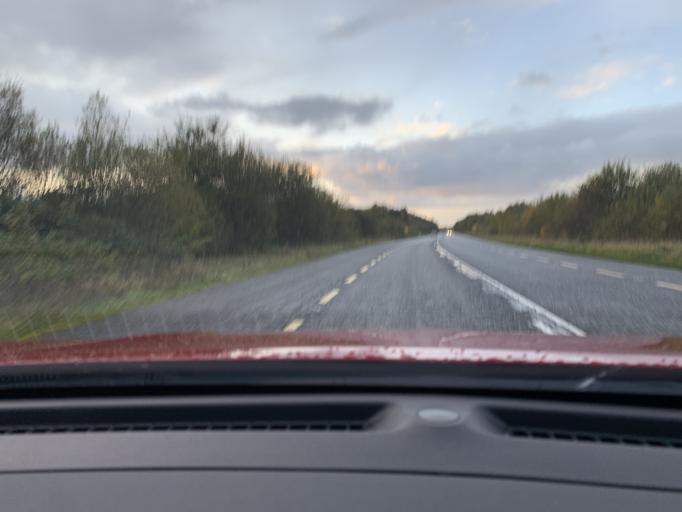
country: IE
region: Connaught
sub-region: County Leitrim
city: Carrick-on-Shannon
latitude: 53.9504
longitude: -8.1493
